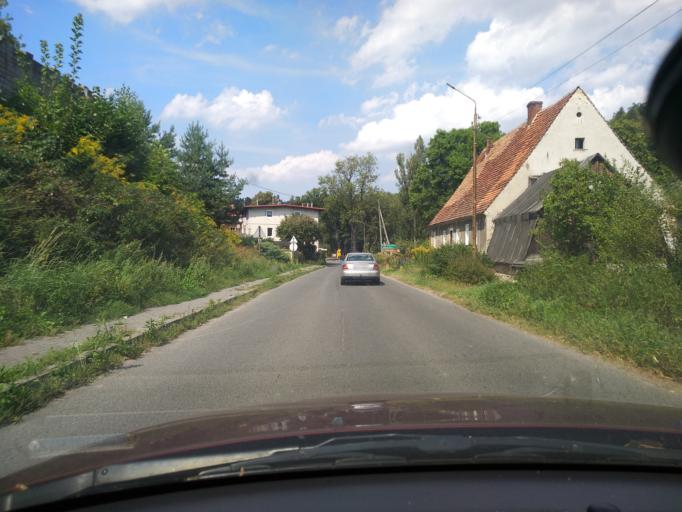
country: PL
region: Lower Silesian Voivodeship
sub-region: Powiat jeleniogorski
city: Stara Kamienica
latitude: 50.9395
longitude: 15.5967
